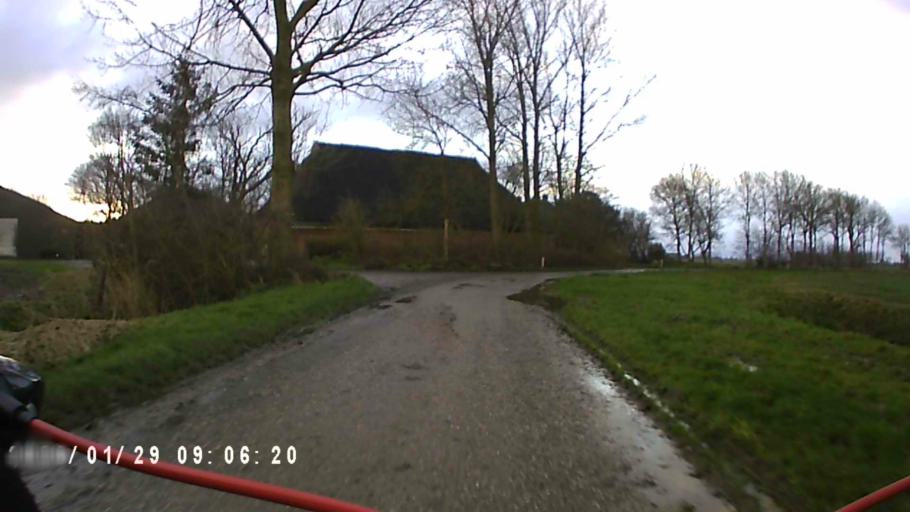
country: NL
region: Groningen
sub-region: Gemeente Zuidhorn
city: Aduard
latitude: 53.3198
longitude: 6.4584
